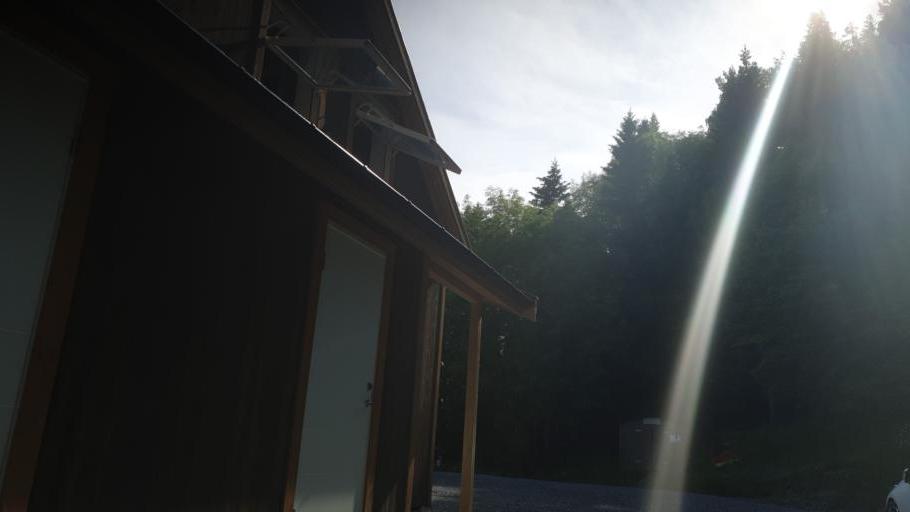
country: NO
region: Nord-Trondelag
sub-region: Leksvik
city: Leksvik
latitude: 63.6794
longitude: 10.6695
